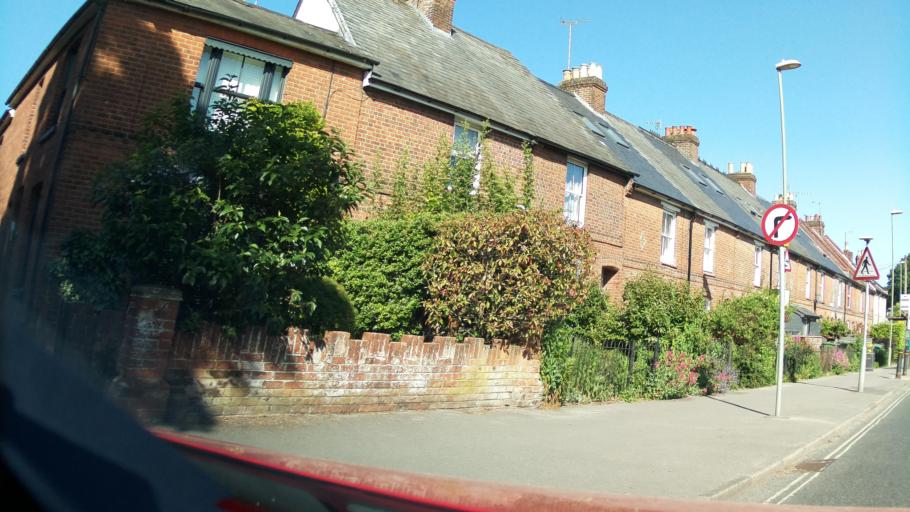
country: GB
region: England
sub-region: Hampshire
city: Winchester
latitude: 51.0678
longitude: -1.3251
